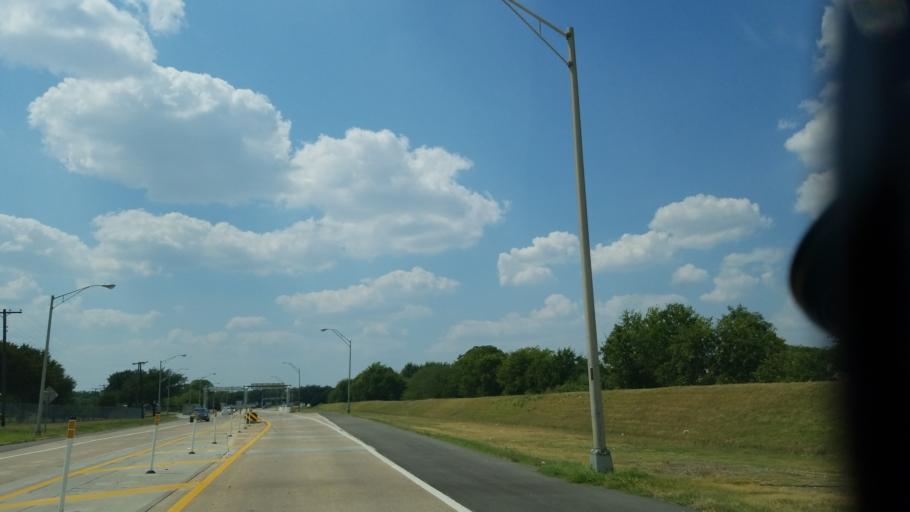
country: US
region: Texas
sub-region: Dallas County
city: Grand Prairie
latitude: 32.7056
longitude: -96.9805
